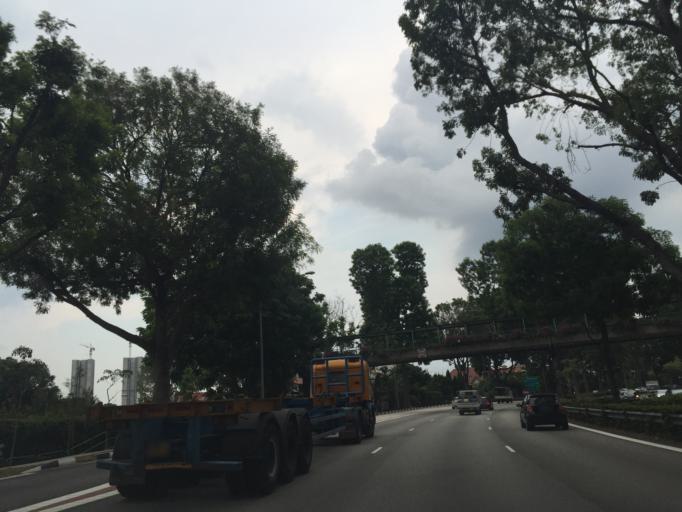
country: SG
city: Singapore
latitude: 1.3213
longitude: 103.7541
